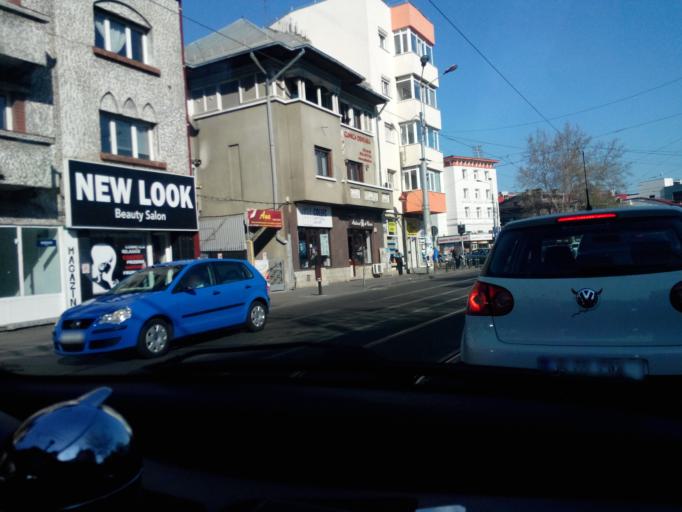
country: RO
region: Bucuresti
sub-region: Municipiul Bucuresti
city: Bucharest
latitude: 44.4525
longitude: 26.1051
